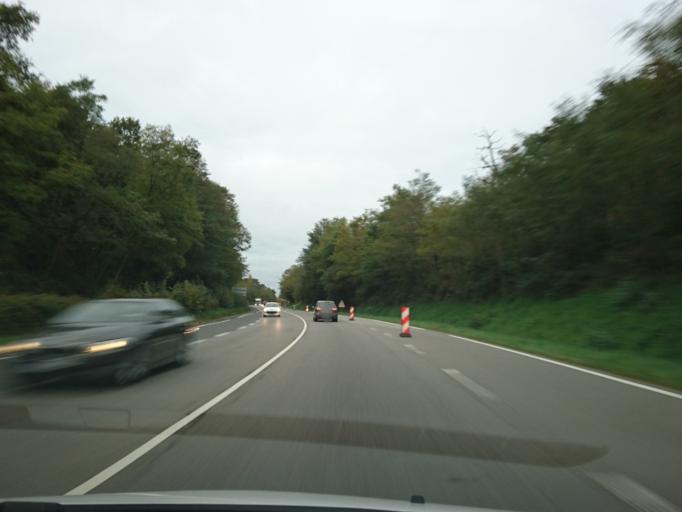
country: FR
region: Pays de la Loire
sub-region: Departement de la Loire-Atlantique
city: Saint-Herblain
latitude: 47.2445
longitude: -1.6356
